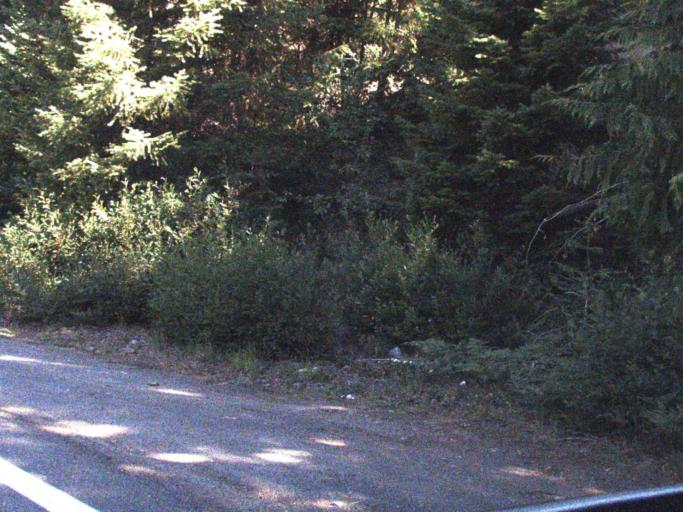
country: US
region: Washington
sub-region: King County
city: Enumclaw
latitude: 46.8879
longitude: -121.5417
